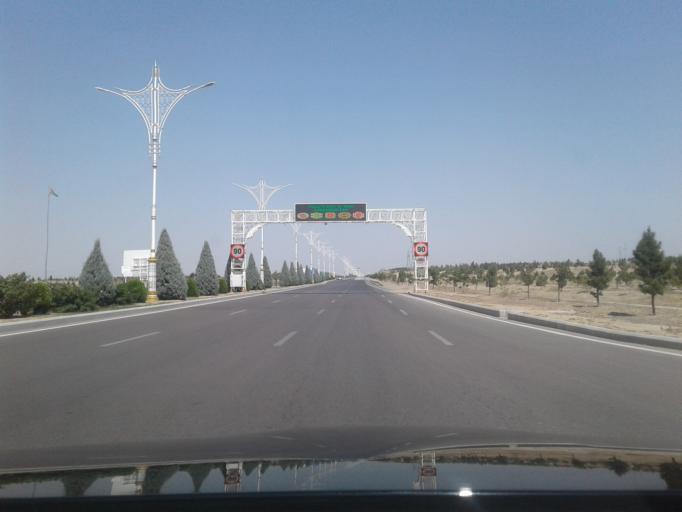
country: TM
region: Ahal
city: Ashgabat
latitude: 37.8786
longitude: 58.3946
